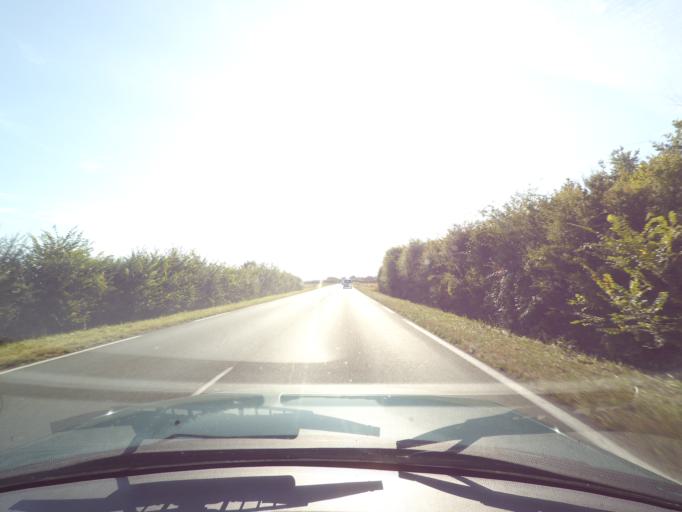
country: FR
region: Poitou-Charentes
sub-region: Departement de la Vienne
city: Ayron
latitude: 46.6611
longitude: 0.0092
